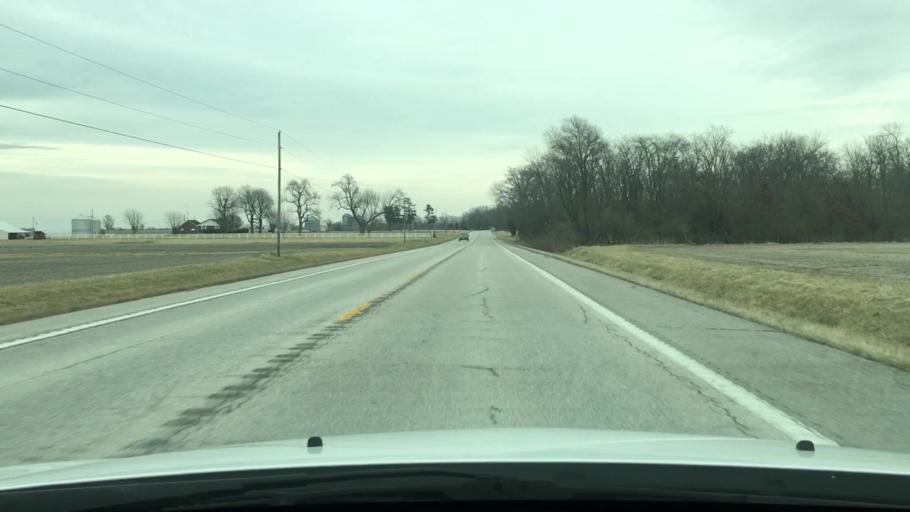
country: US
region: Missouri
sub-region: Audrain County
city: Vandalia
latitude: 39.2790
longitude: -91.5679
